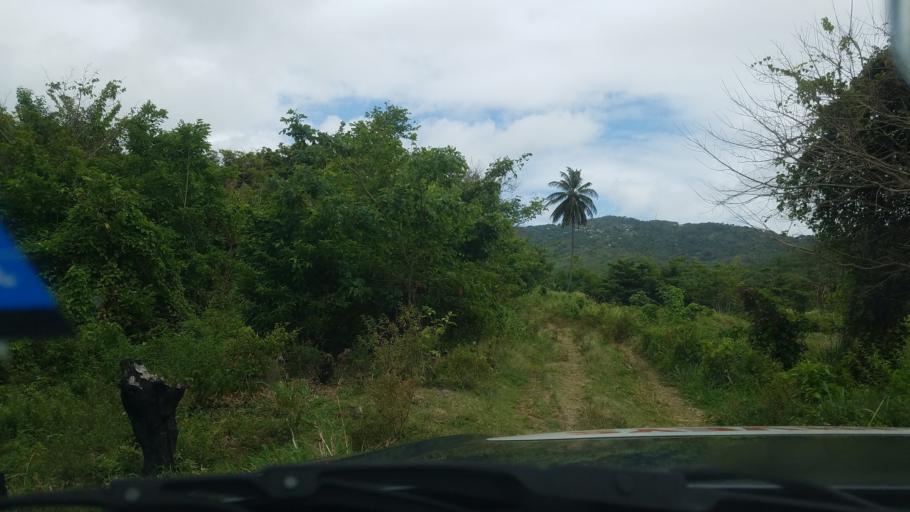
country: LC
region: Gros-Islet
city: Gros Islet
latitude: 14.0296
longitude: -60.9022
